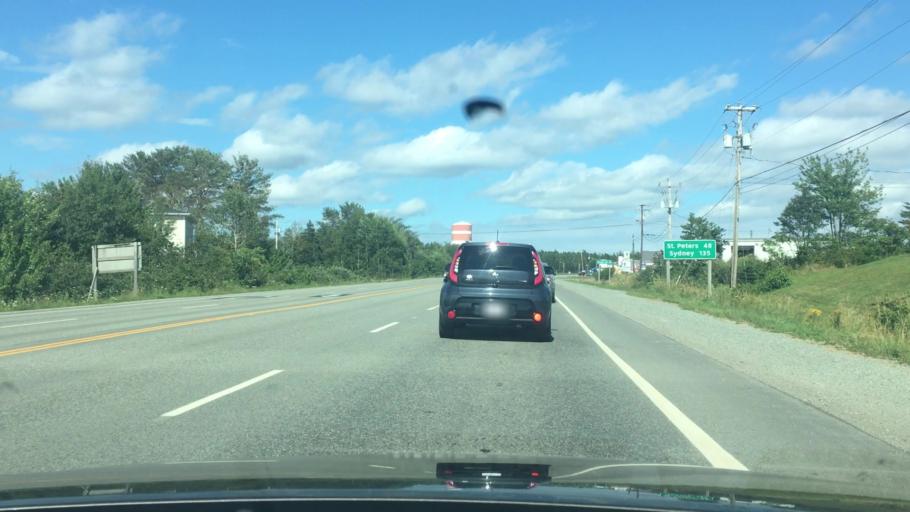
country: CA
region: Nova Scotia
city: Port Hawkesbury
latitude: 45.6124
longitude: -61.3443
